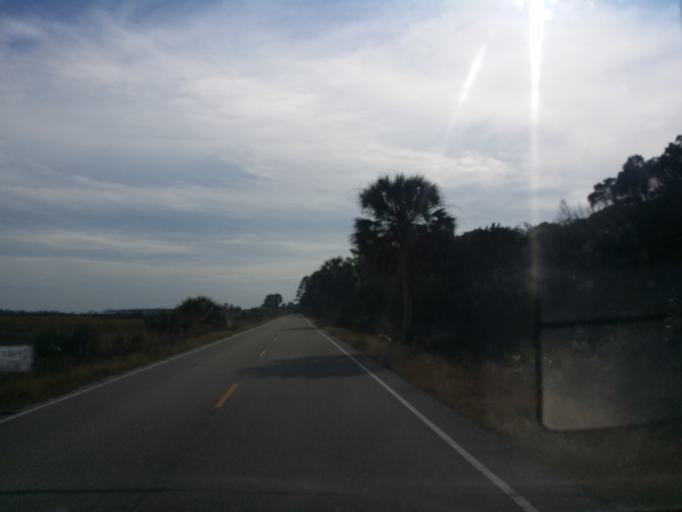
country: US
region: Florida
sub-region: Leon County
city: Woodville
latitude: 30.1152
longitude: -84.1489
